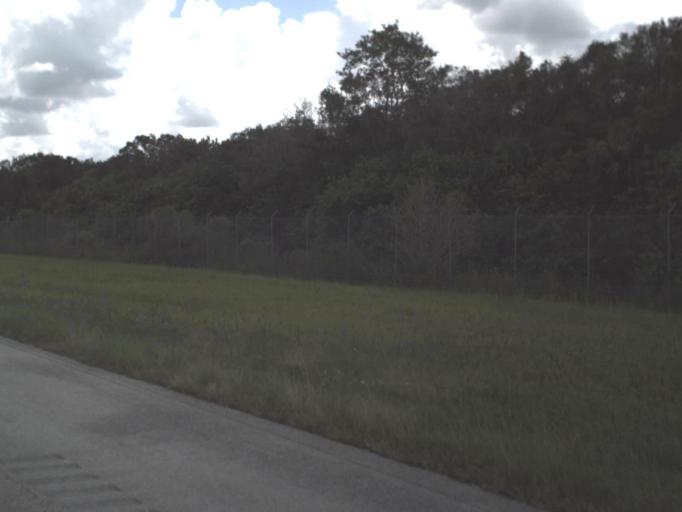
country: US
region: Florida
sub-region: Collier County
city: Orangetree
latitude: 26.1530
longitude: -81.5107
